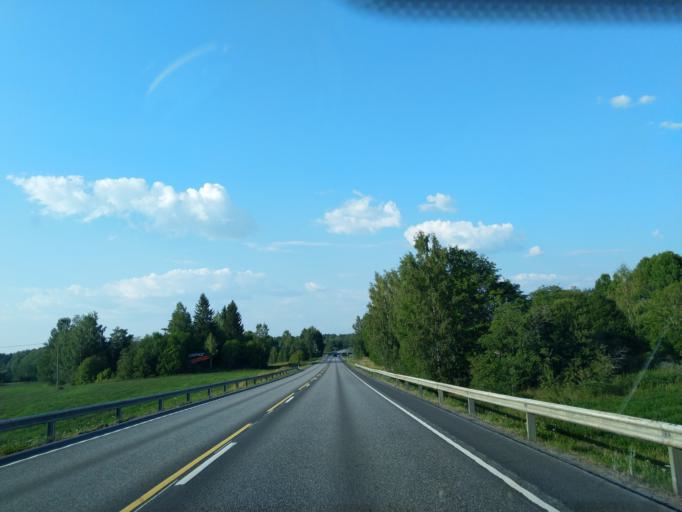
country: FI
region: Satakunta
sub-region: Pori
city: Pomarkku
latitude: 61.6932
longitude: 22.0024
